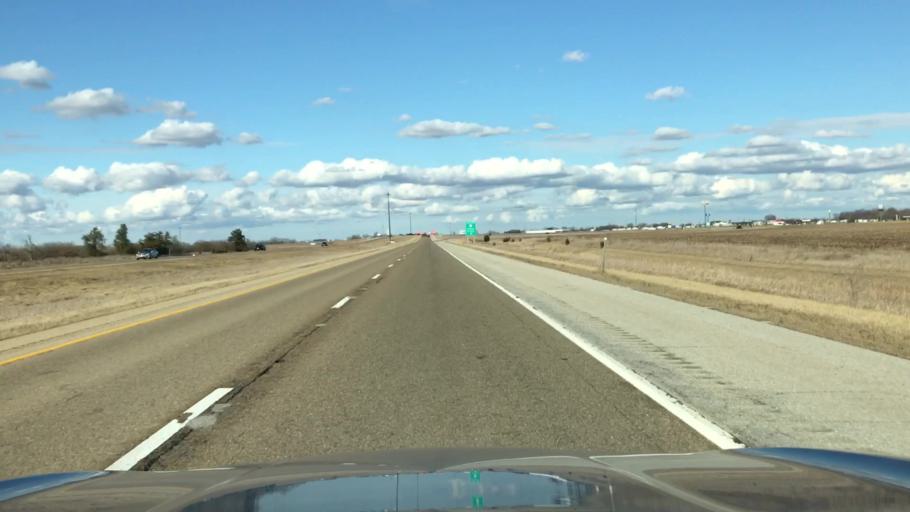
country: US
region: Illinois
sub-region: McLean County
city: Chenoa
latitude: 40.7324
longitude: -88.7372
